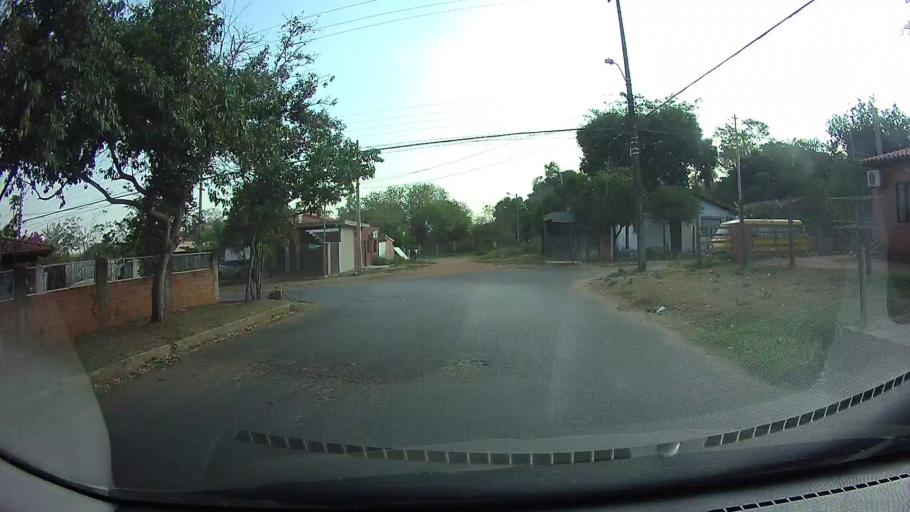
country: PY
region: Central
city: Limpio
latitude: -25.2072
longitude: -57.5083
